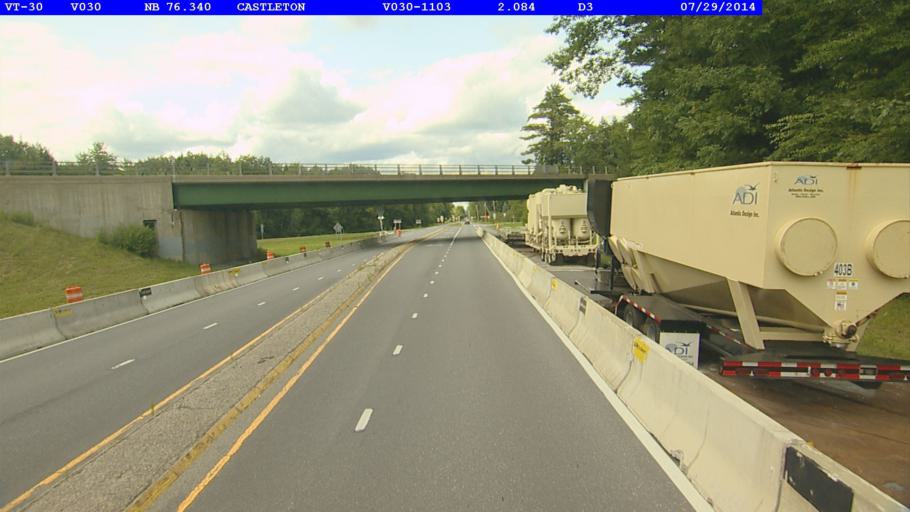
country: US
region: Vermont
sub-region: Rutland County
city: Castleton
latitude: 43.6167
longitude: -73.2066
